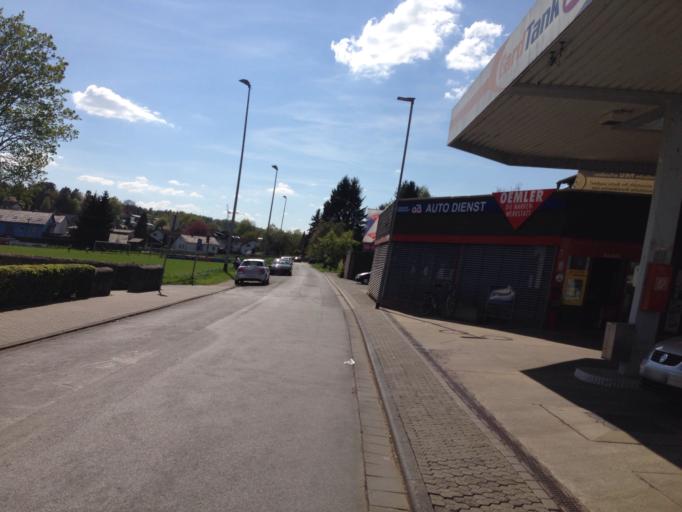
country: DE
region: Hesse
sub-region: Regierungsbezirk Giessen
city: Laubach
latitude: 50.5485
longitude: 8.9557
